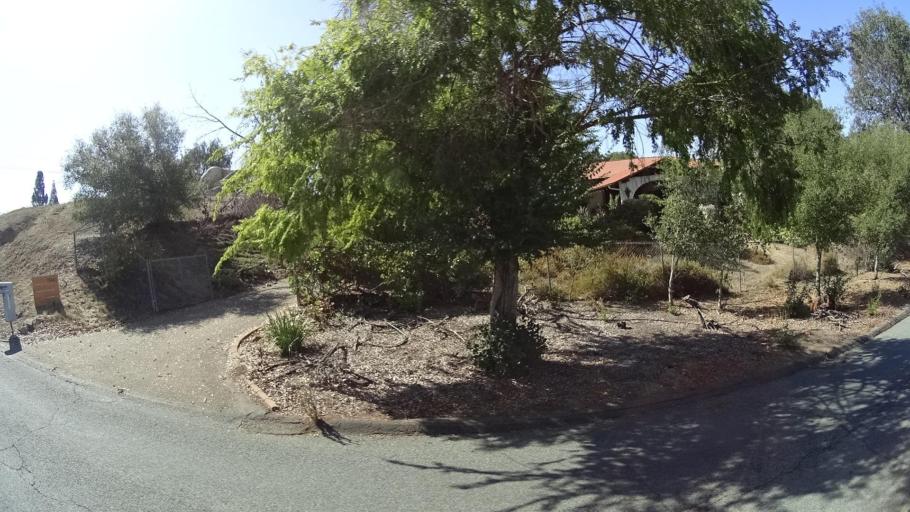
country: US
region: California
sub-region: San Diego County
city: Granite Hills
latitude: 32.7897
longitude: -116.9111
